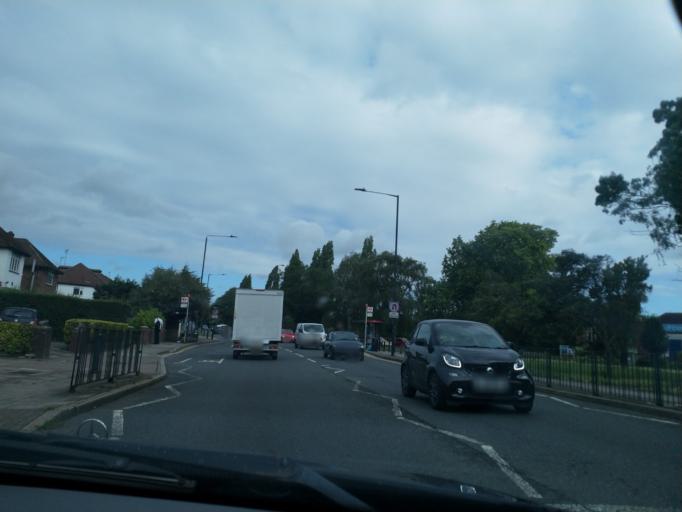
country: GB
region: England
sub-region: Greater London
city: Harrow on the Hill
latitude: 51.5686
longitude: -0.3215
